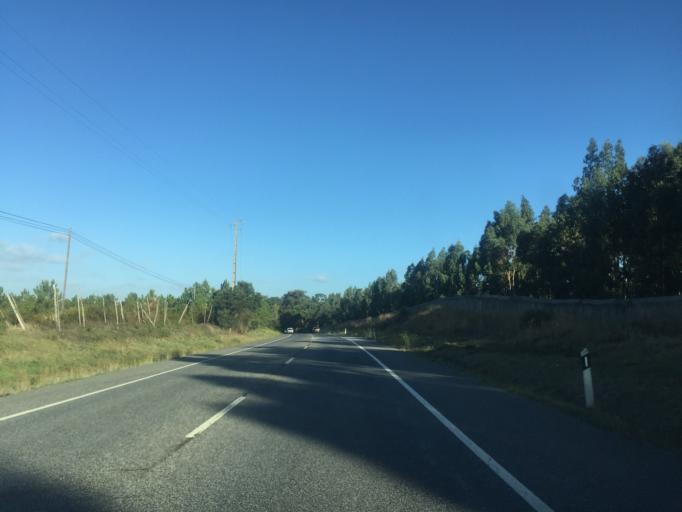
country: PT
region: Lisbon
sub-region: Azambuja
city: Alcoentre
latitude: 39.1815
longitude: -8.9395
